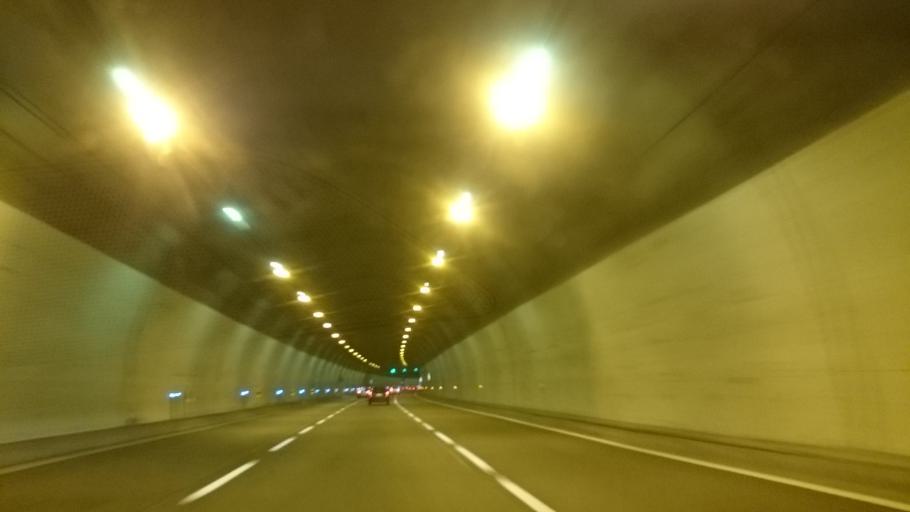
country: IT
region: Emilia-Romagna
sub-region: Provincia di Bologna
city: Vado
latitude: 44.3131
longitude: 11.2508
